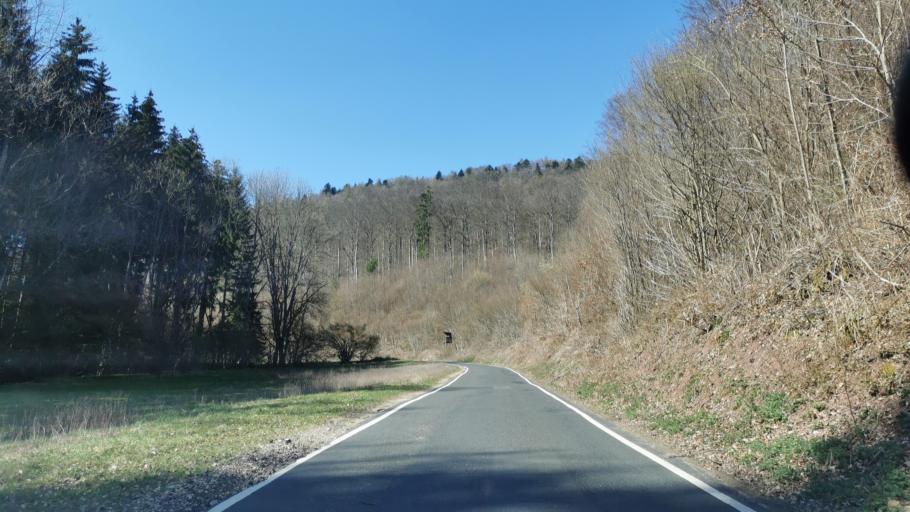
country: DE
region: Rheinland-Pfalz
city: Aach
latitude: 49.7829
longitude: 6.6050
